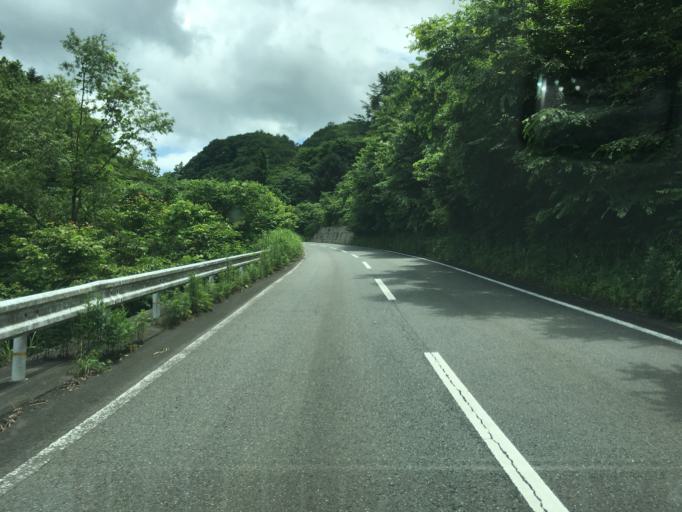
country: JP
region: Miyagi
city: Marumori
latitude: 37.7090
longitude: 140.8778
